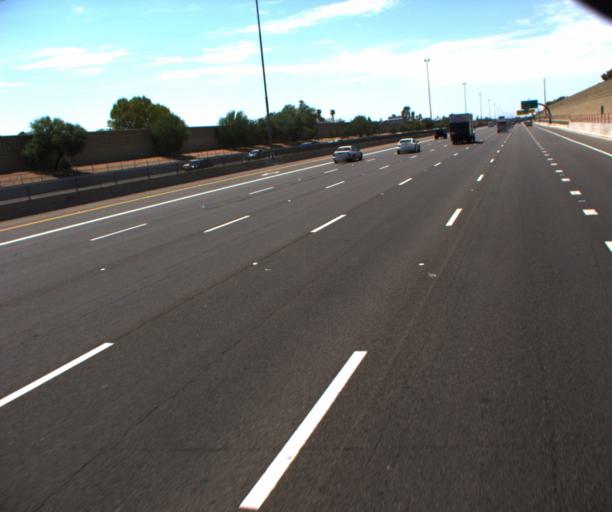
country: US
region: Arizona
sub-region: Maricopa County
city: Tempe
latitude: 33.3859
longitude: -111.9153
